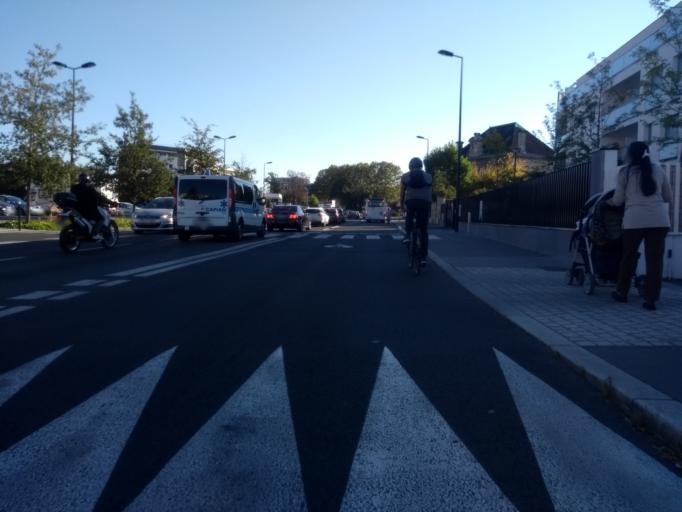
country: FR
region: Aquitaine
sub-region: Departement de la Gironde
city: Talence
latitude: 44.8199
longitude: -0.6022
